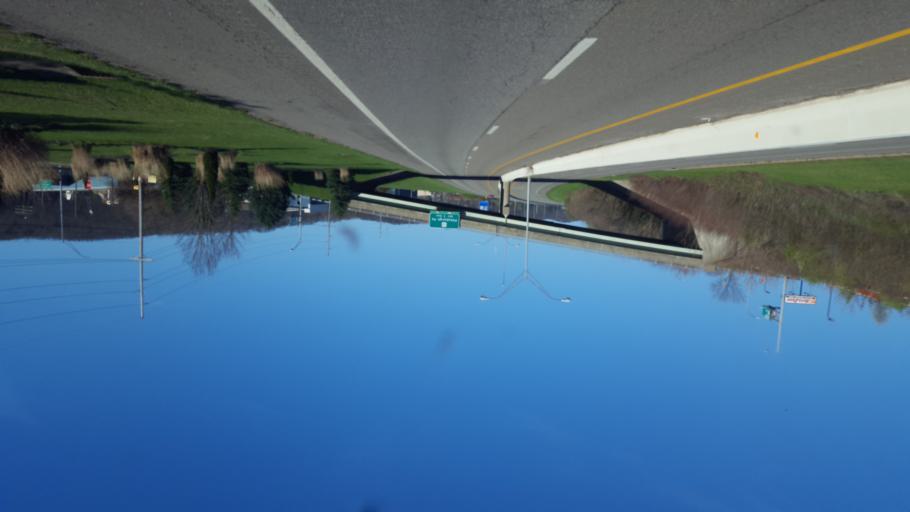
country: US
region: Ohio
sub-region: Columbiana County
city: East Liverpool
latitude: 40.6182
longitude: -80.5842
